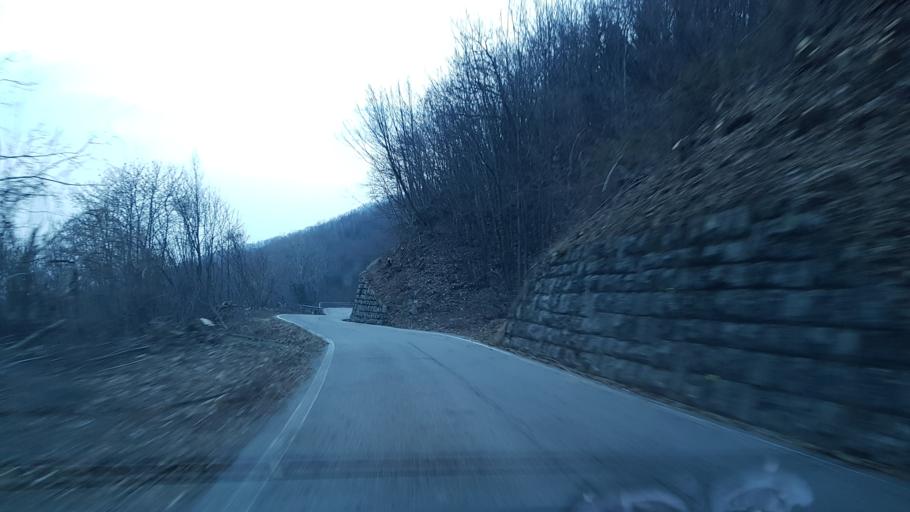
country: IT
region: Friuli Venezia Giulia
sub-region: Provincia di Udine
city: Attimis
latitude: 46.2040
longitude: 13.3427
